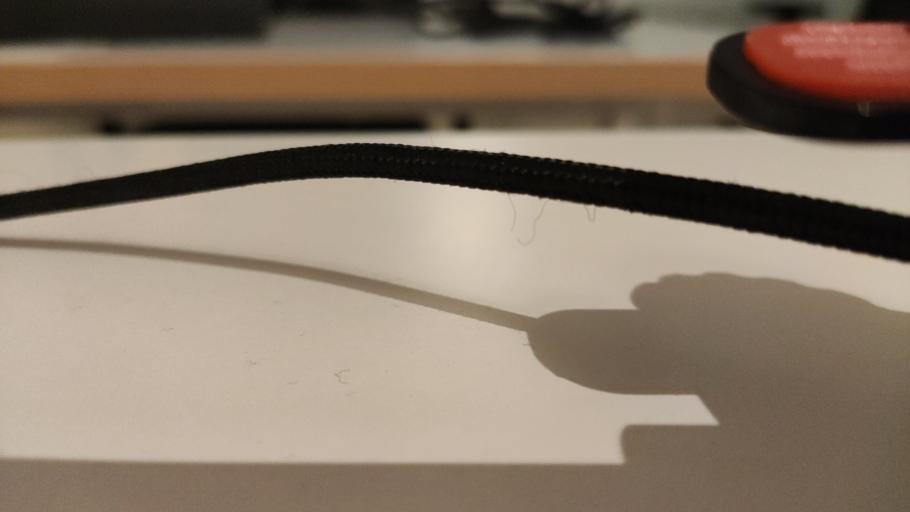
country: RU
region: Moskovskaya
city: Orekhovo-Zuyevo
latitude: 55.8209
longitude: 38.9662
